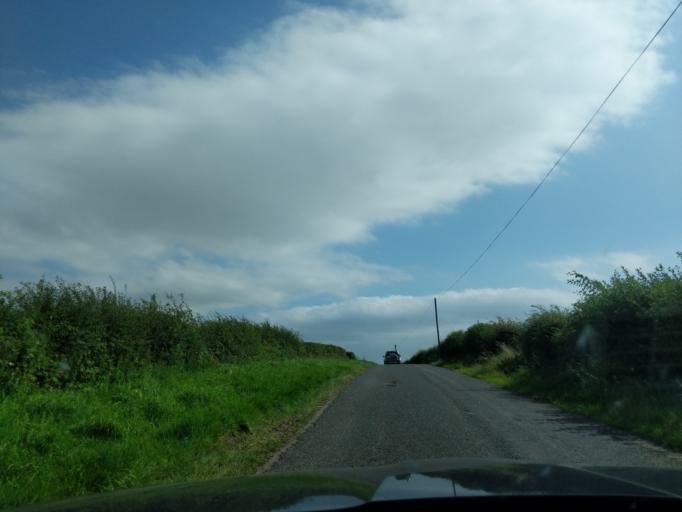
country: GB
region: England
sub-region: Northumberland
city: Ford
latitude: 55.6543
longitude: -2.1479
